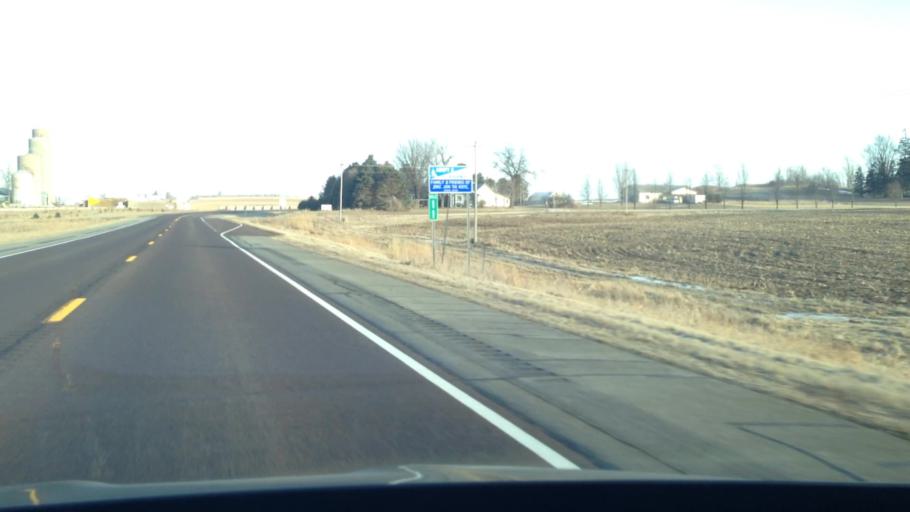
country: US
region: Minnesota
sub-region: Goodhue County
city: Goodhue
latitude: 44.4251
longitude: -92.6212
